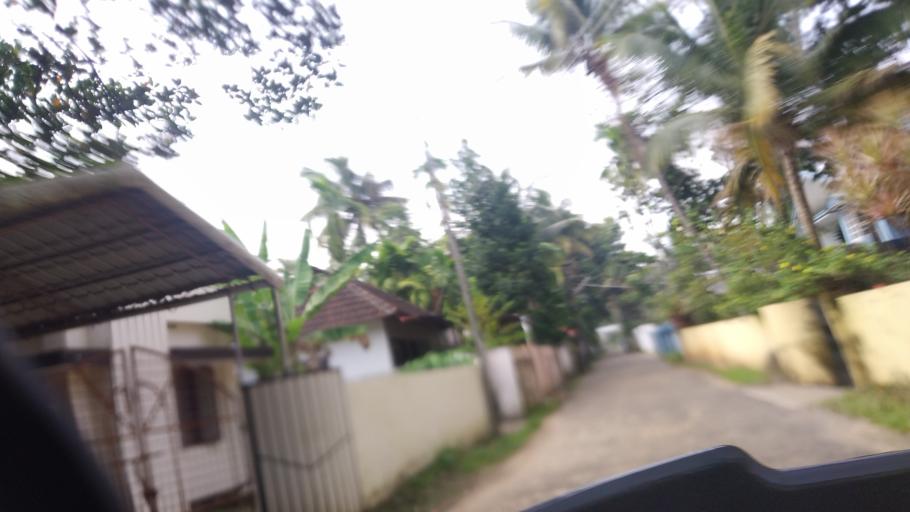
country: IN
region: Kerala
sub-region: Ernakulam
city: Elur
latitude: 10.0519
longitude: 76.2178
